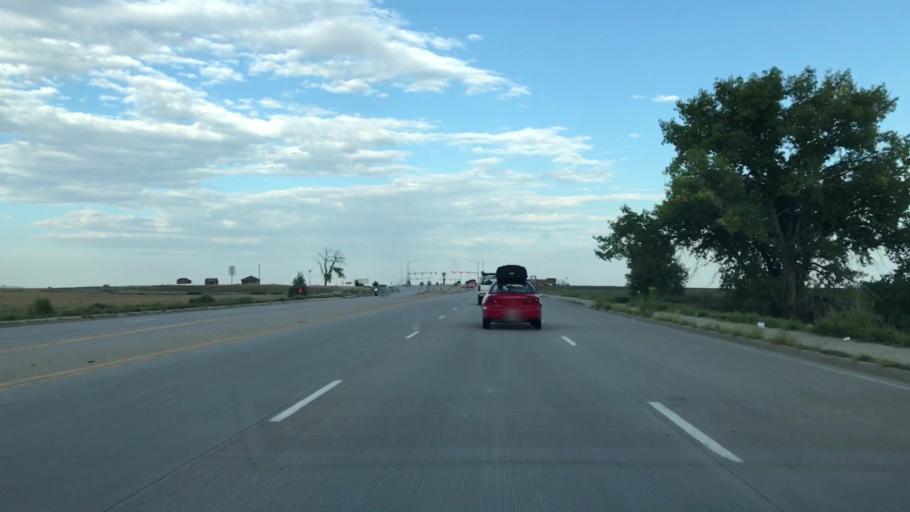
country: US
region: Colorado
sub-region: Weld County
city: Mead
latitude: 40.2042
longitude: -104.9862
